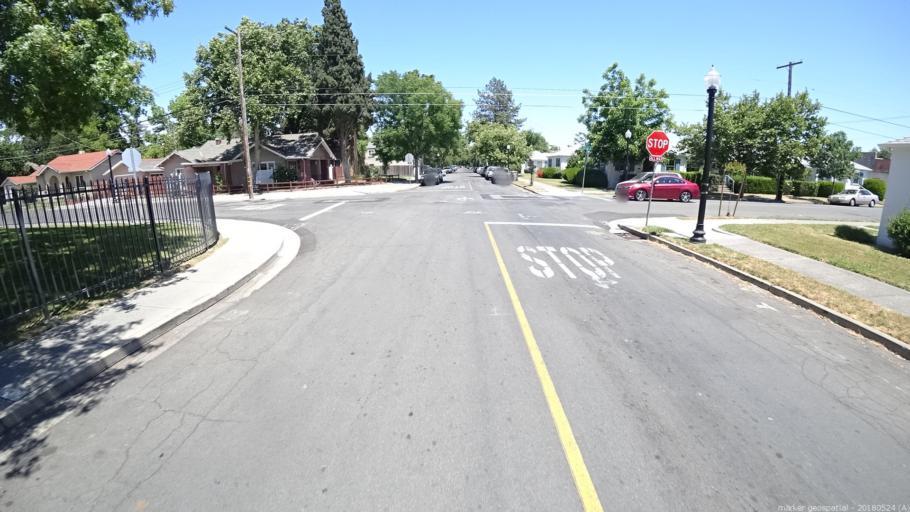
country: US
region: California
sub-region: Sacramento County
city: Sacramento
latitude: 38.6090
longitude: -121.4558
